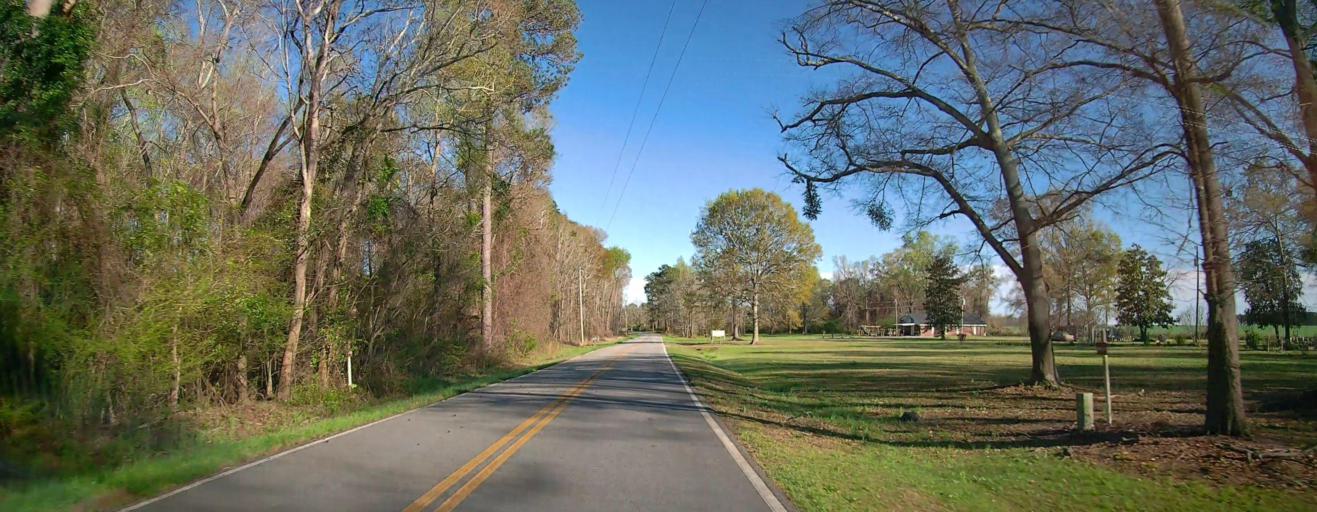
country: US
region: Georgia
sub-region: Houston County
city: Perry
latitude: 32.3632
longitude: -83.6560
